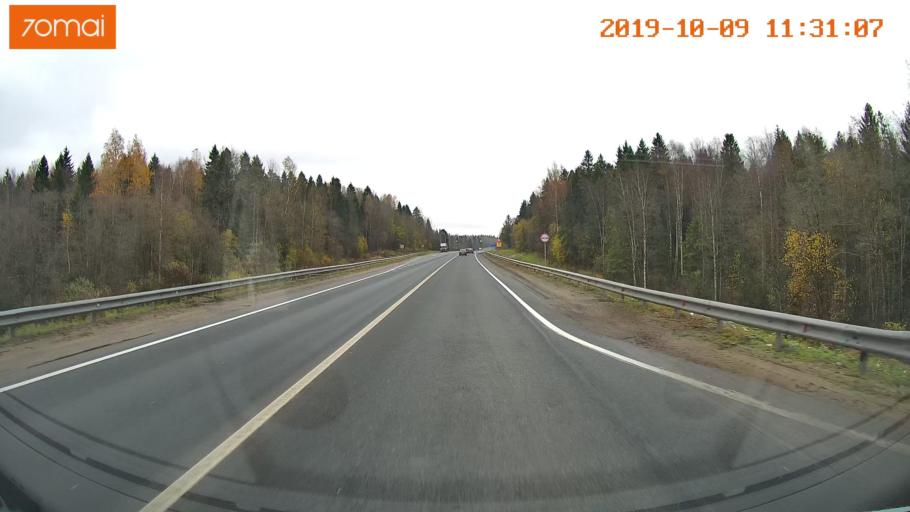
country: RU
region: Vologda
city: Gryazovets
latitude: 59.0482
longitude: 40.0894
